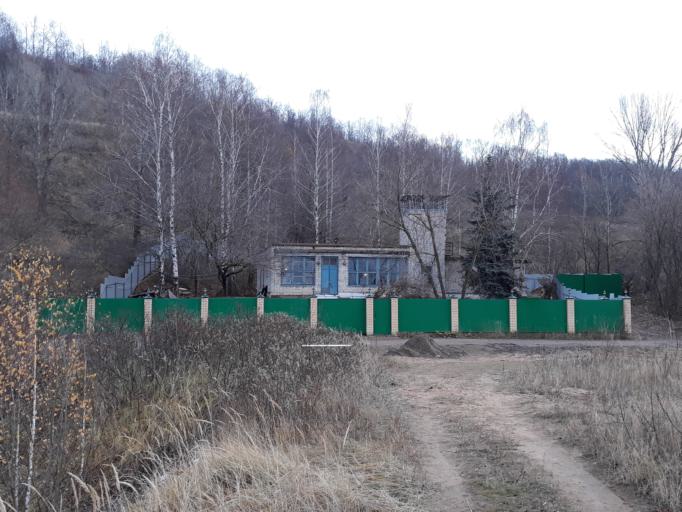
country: RU
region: Nizjnij Novgorod
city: Nizhniy Novgorod
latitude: 56.2668
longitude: 43.9693
